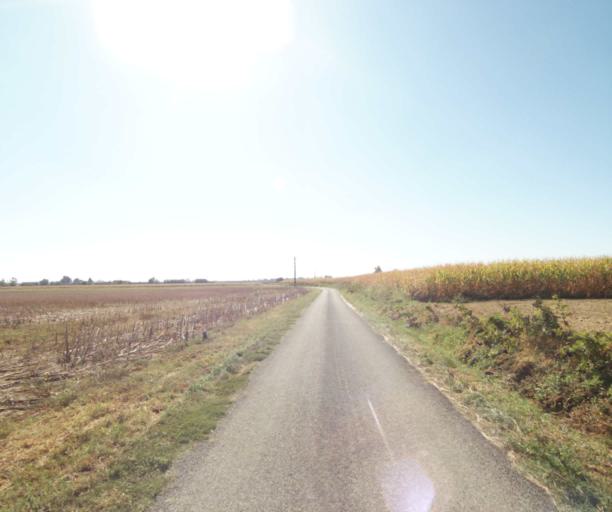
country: FR
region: Midi-Pyrenees
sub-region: Departement du Tarn-et-Garonne
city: Verdun-sur-Garonne
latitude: 43.8211
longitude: 1.2140
